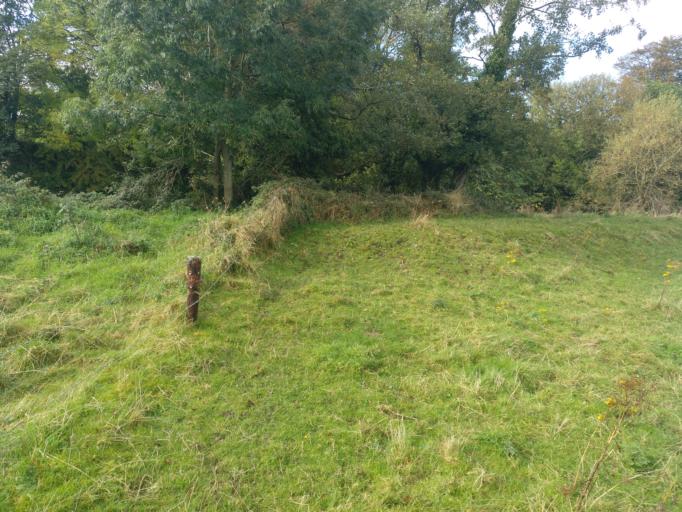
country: IE
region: Leinster
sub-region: Kilkenny
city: Castlecomer
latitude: 52.7938
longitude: -7.2074
